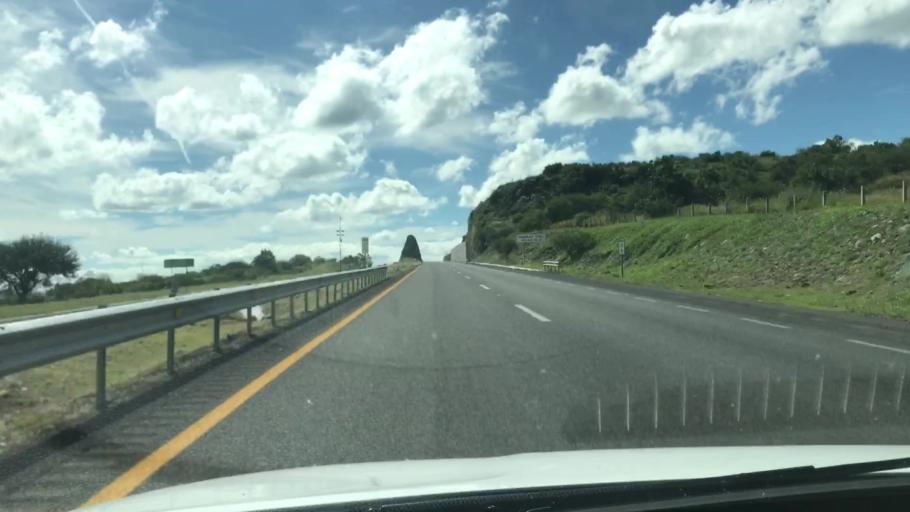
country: MX
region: Guanajuato
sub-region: Silao de la Victoria
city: Bajio de Bonillas
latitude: 20.9565
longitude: -101.5142
